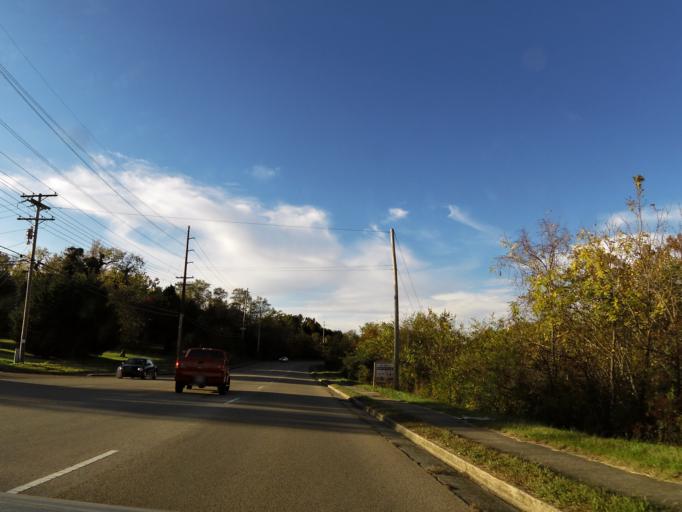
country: US
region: Tennessee
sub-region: Blount County
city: Louisville
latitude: 35.8685
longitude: -84.0635
